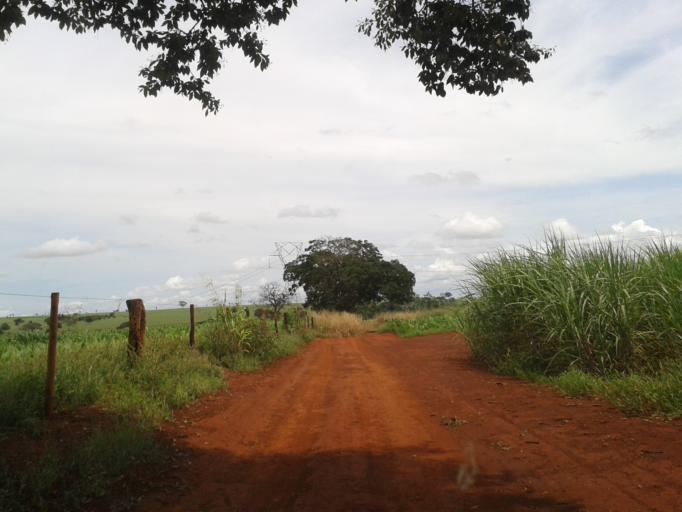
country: BR
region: Minas Gerais
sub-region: Centralina
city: Centralina
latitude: -18.6127
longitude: -49.2915
